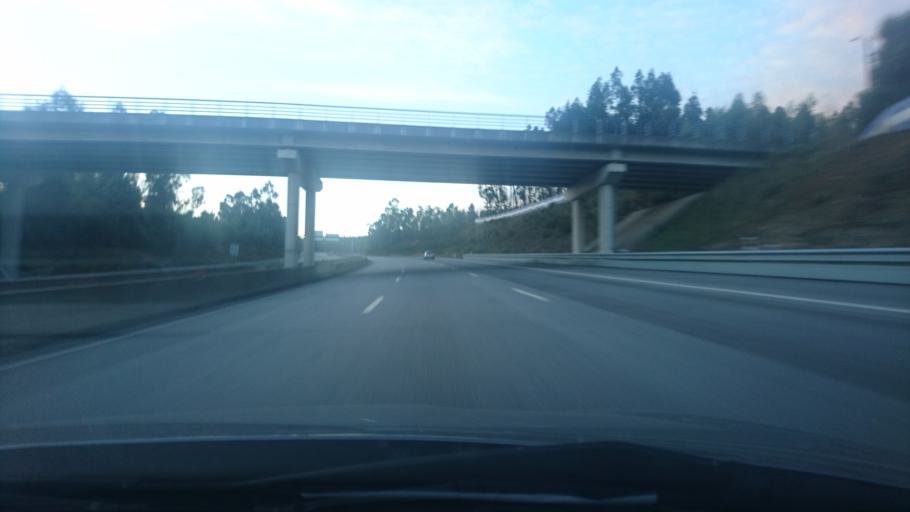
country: PT
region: Aveiro
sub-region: Santa Maria da Feira
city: Lobao
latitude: 40.9805
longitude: -8.4674
